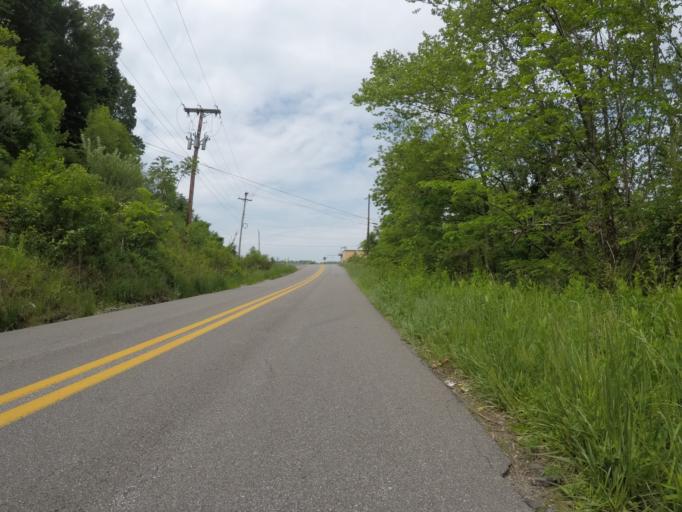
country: US
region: West Virginia
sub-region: Wayne County
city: Kenova
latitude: 38.3355
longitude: -82.5793
